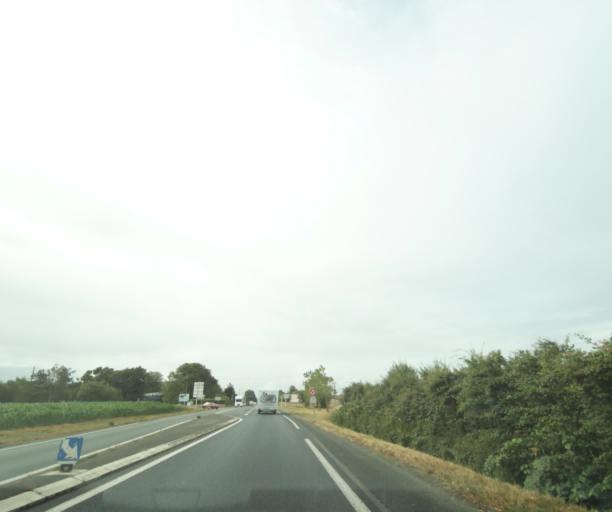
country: FR
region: Pays de la Loire
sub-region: Departement de la Vendee
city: Sainte-Gemme-la-Plaine
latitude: 46.4525
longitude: -1.1043
